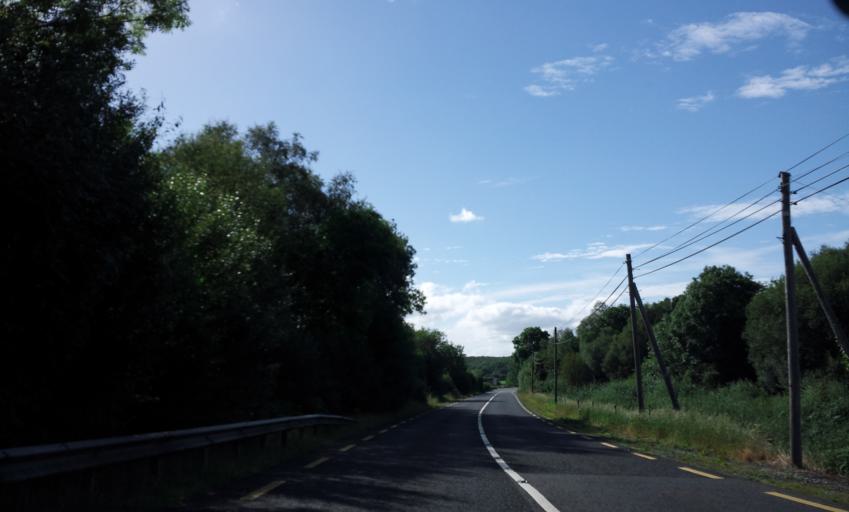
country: IE
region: Munster
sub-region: County Cork
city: Macroom
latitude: 51.9104
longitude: -9.0429
